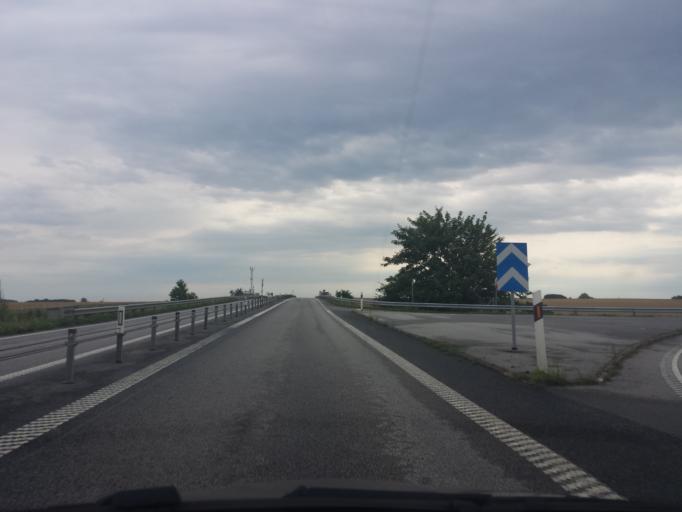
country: SE
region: Skane
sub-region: Skurups Kommun
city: Rydsgard
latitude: 55.4742
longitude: 13.6663
